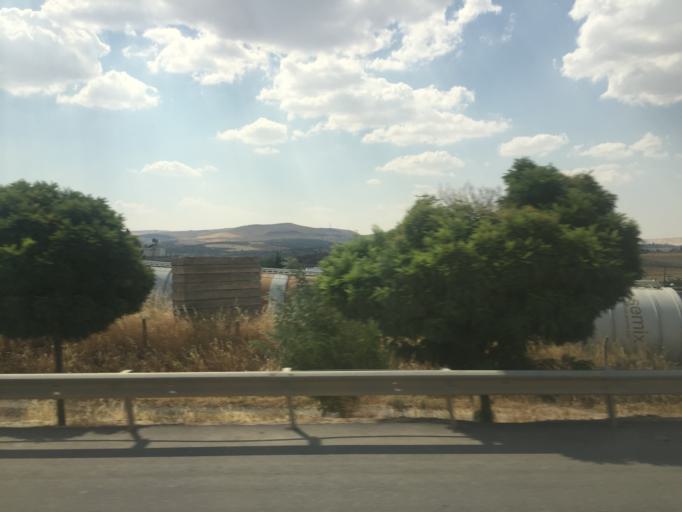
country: TR
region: Sanliurfa
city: Sanliurfa
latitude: 37.2552
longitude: 38.7927
